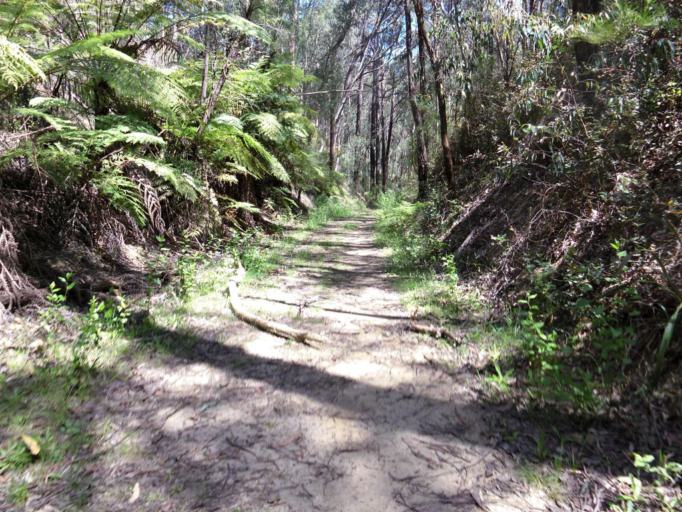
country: AU
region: Victoria
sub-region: Baw Baw
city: Warragul
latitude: -37.9025
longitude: 145.9799
